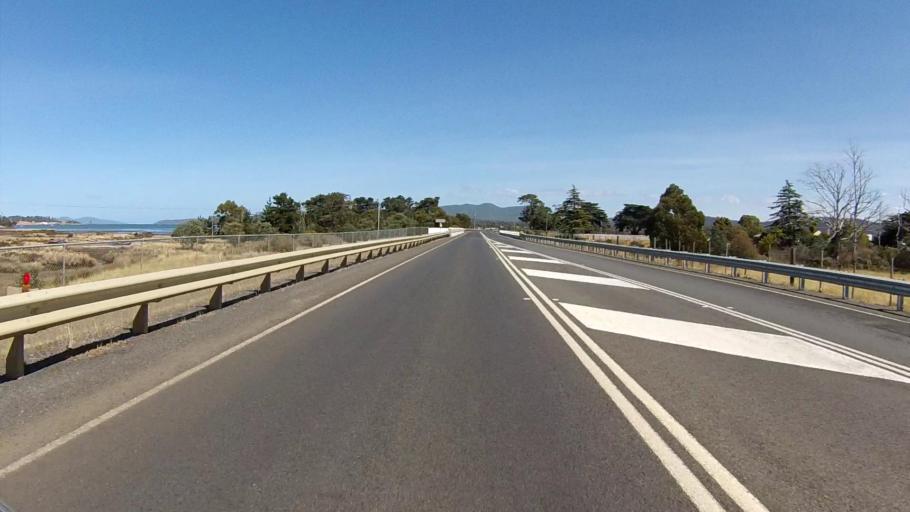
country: AU
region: Tasmania
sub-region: Sorell
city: Sorell
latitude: -42.5088
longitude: 147.9084
